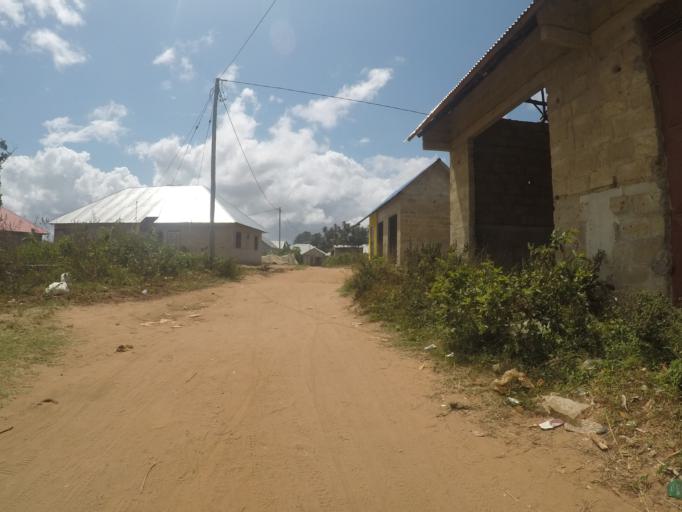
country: TZ
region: Zanzibar Urban/West
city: Zanzibar
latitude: -6.2014
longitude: 39.2352
